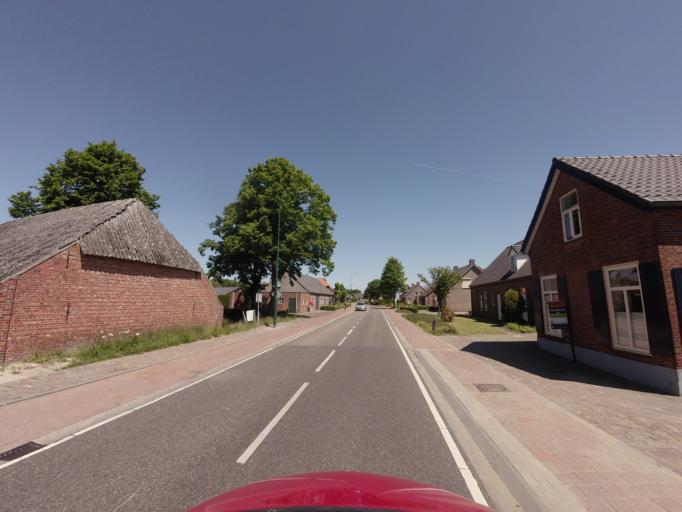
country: BE
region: Flanders
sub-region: Provincie Limburg
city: Lommel
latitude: 51.2834
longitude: 5.3136
